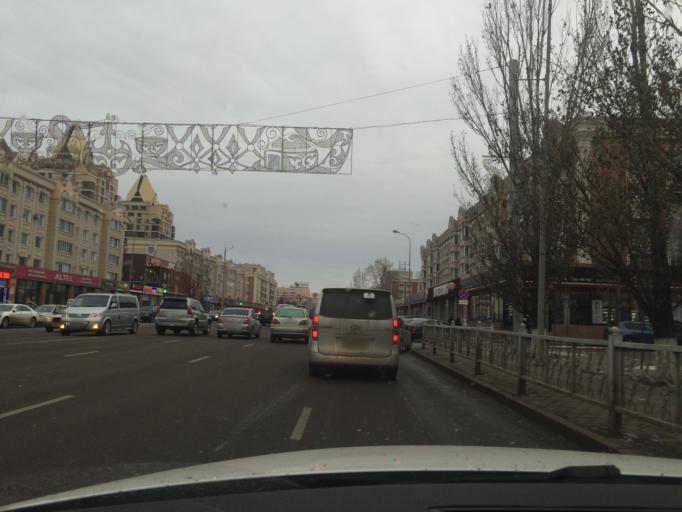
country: KZ
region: Astana Qalasy
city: Astana
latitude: 51.1587
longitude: 71.4294
